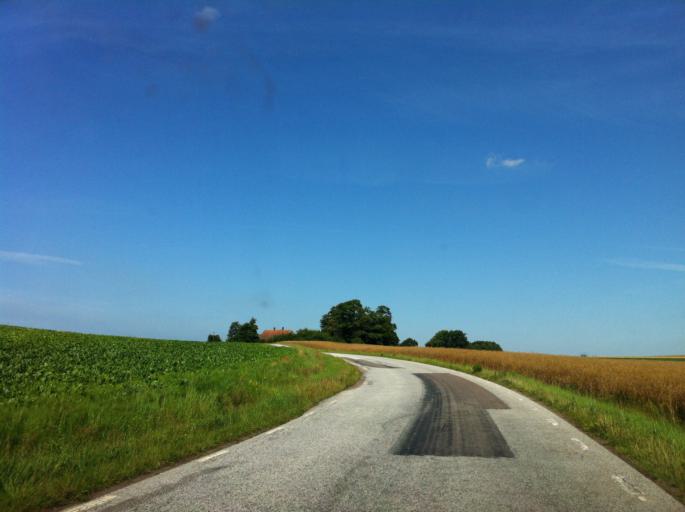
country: SE
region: Skane
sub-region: Landskrona
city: Asmundtorp
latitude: 55.9254
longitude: 12.8930
